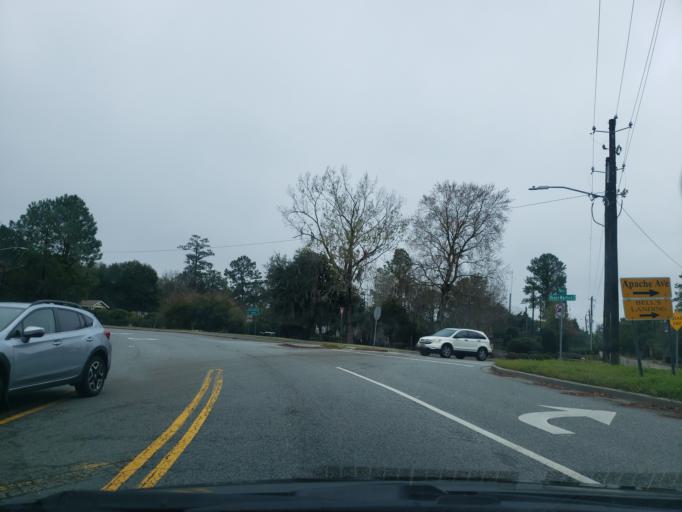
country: US
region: Georgia
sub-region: Chatham County
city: Georgetown
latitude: 31.9777
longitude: -81.1703
